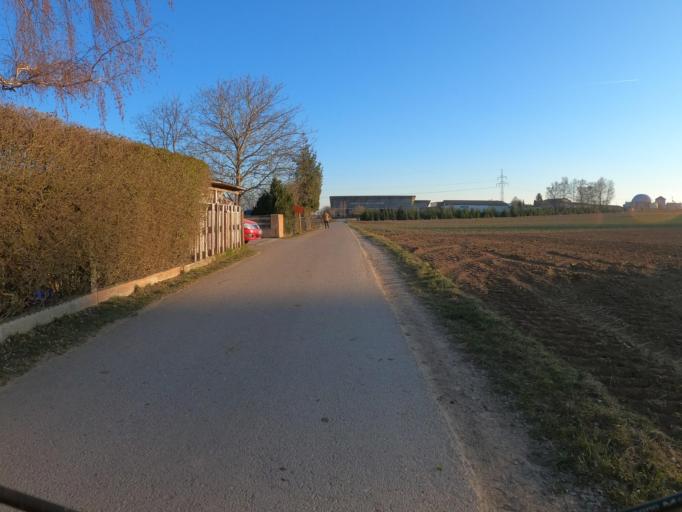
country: DE
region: Baden-Wuerttemberg
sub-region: Tuebingen Region
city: Langenau
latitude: 48.4871
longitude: 10.1131
